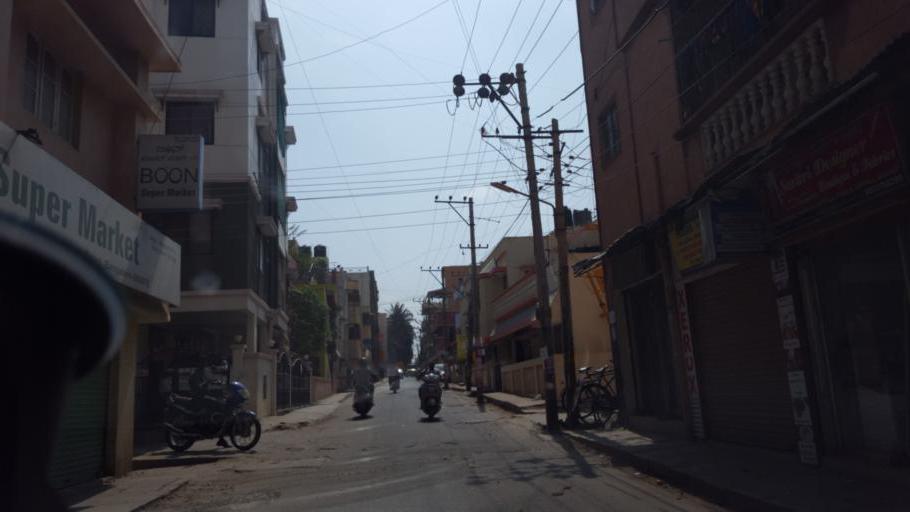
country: IN
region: Karnataka
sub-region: Bangalore Urban
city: Bangalore
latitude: 12.9764
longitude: 77.6737
